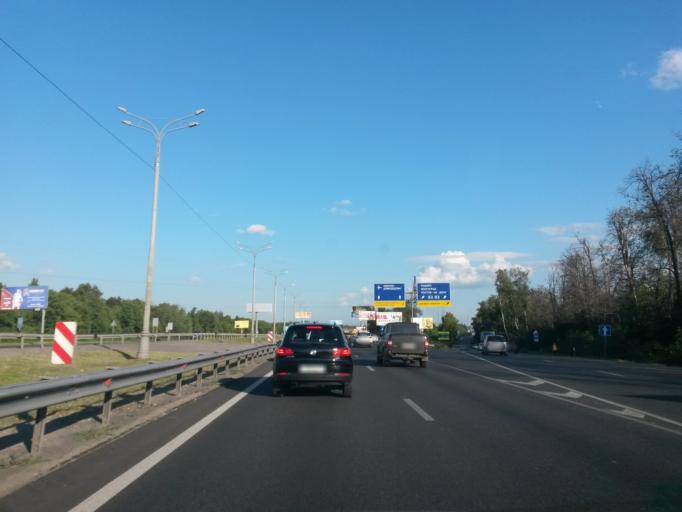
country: RU
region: Moskovskaya
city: Razvilka
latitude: 55.5808
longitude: 37.7500
